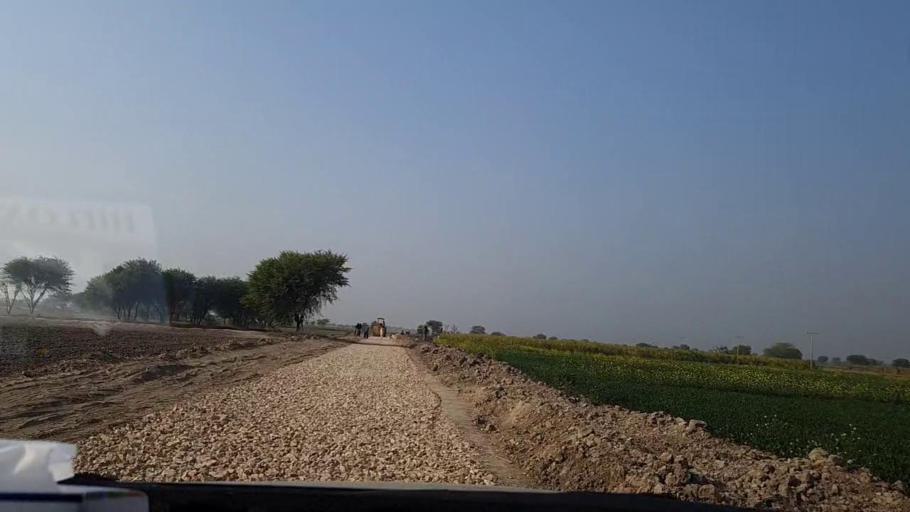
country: PK
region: Sindh
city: Tando Ghulam Ali
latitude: 25.1946
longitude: 68.8766
